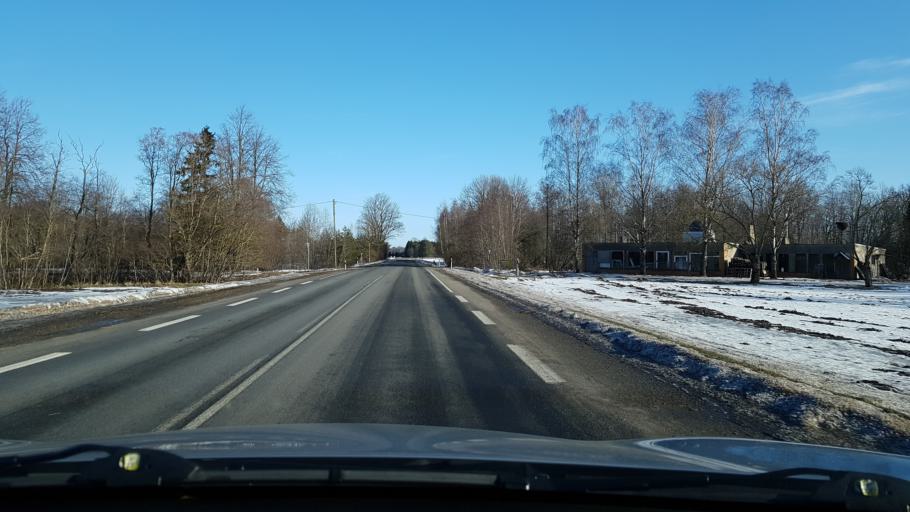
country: EE
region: Viljandimaa
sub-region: Vohma linn
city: Vohma
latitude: 58.6328
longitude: 25.6449
